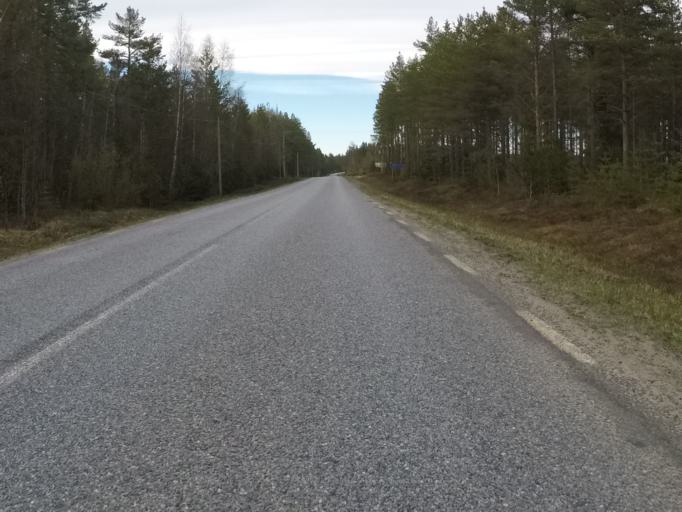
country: SE
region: Vaesterbotten
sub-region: Umea Kommun
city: Saevar
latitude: 63.9480
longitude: 20.7914
